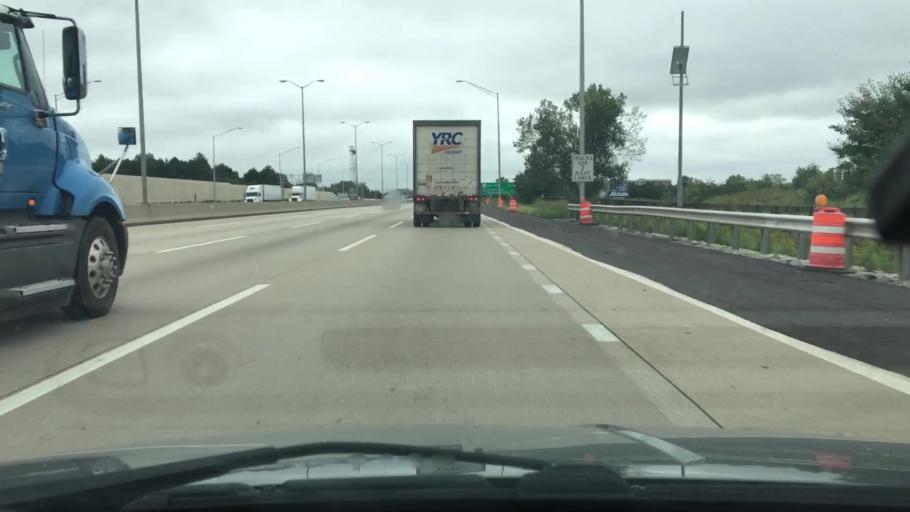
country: US
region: Illinois
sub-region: Cook County
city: Northbrook
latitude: 42.0983
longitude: -87.8683
